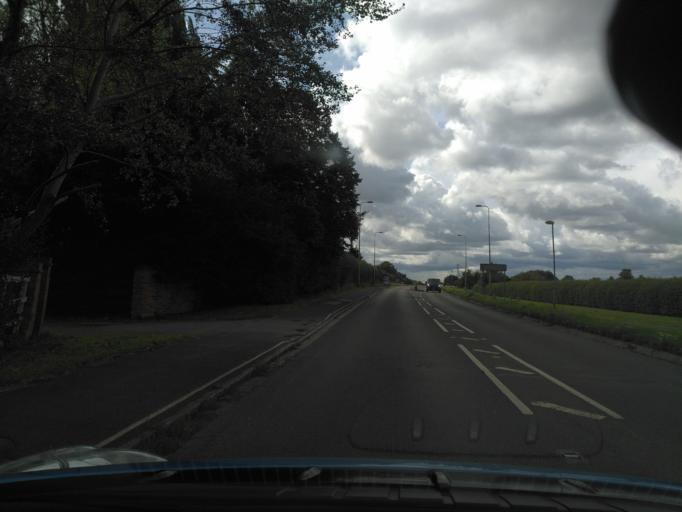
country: GB
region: England
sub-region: Oxfordshire
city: Radley
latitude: 51.6530
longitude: -1.2297
